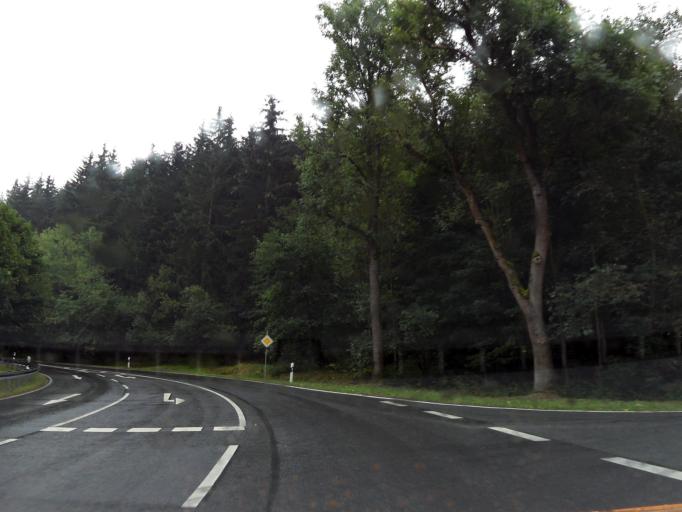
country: DE
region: Saxony-Anhalt
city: Harzgerode
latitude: 51.6439
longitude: 11.1089
